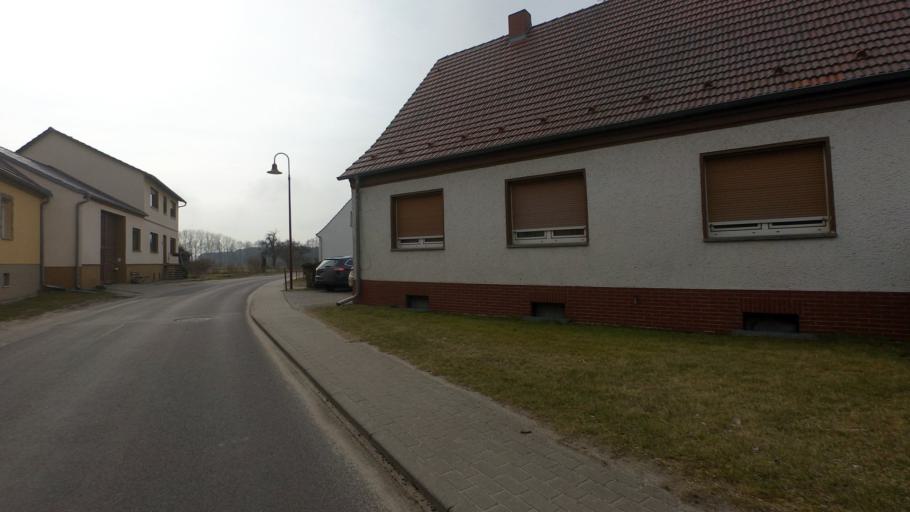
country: DE
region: Brandenburg
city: Borkheide
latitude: 52.1874
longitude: 12.8714
